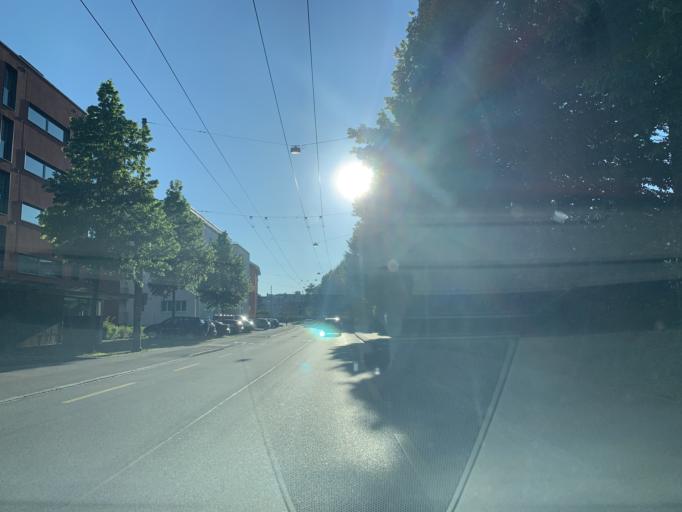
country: CH
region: Zurich
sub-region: Bezirk Winterthur
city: Seen (Kreis 3) / Waser
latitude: 47.4871
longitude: 8.7615
